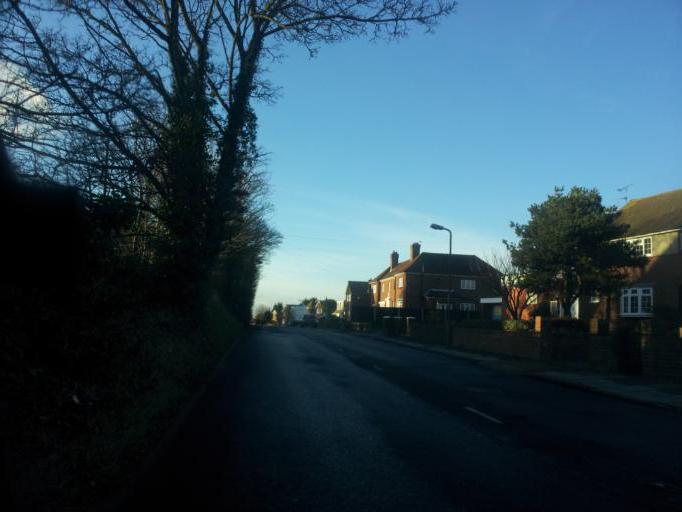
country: GB
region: England
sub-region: Kent
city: Gravesend
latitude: 51.4127
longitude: 0.3739
